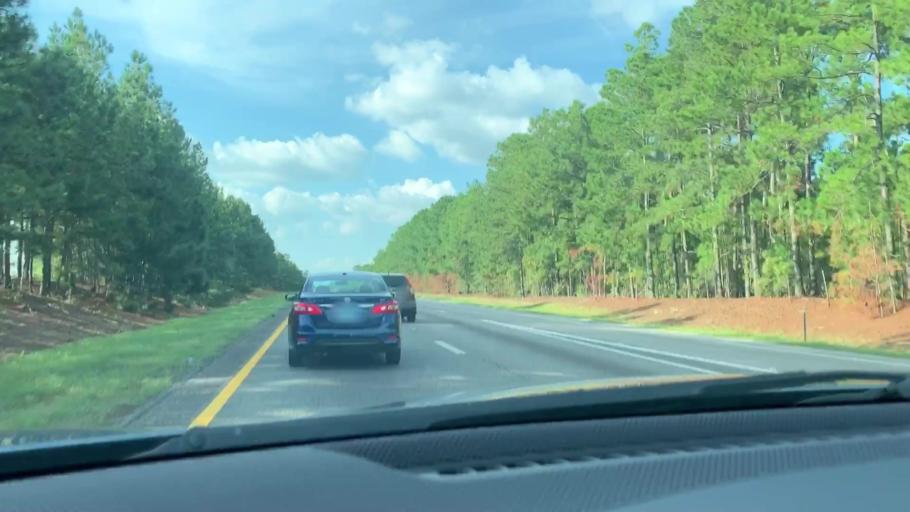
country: US
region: South Carolina
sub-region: Calhoun County
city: Saint Matthews
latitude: 33.6369
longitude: -80.8768
